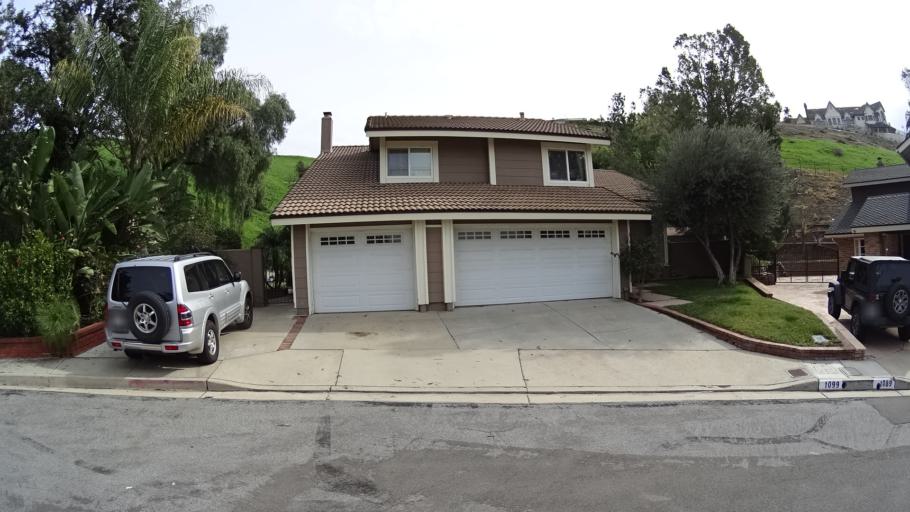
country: US
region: California
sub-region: Orange County
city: Villa Park
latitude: 33.8378
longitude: -117.7426
